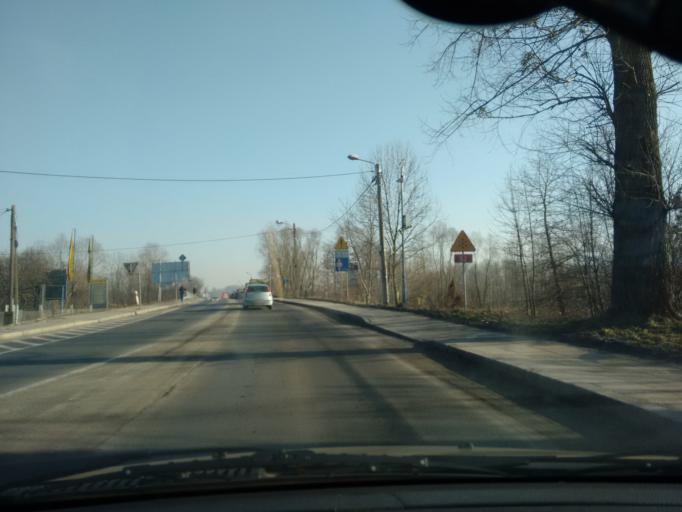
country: PL
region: Lesser Poland Voivodeship
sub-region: Powiat wadowicki
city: Wadowice
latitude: 49.8772
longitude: 19.5081
